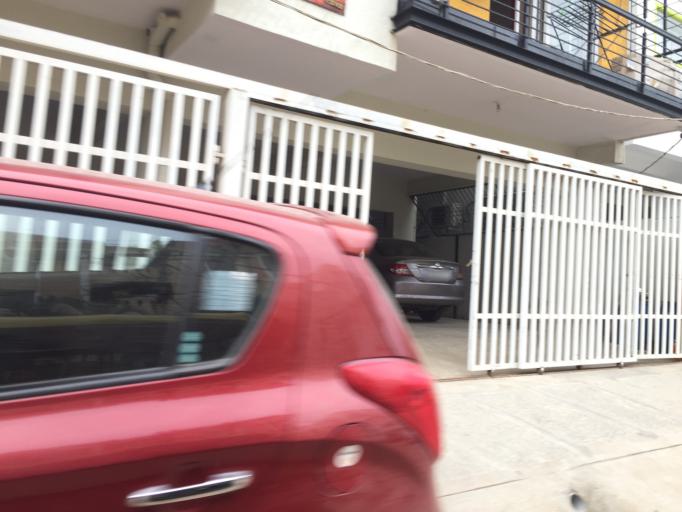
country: IN
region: Karnataka
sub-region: Bangalore Urban
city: Bangalore
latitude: 12.9622
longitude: 77.6574
